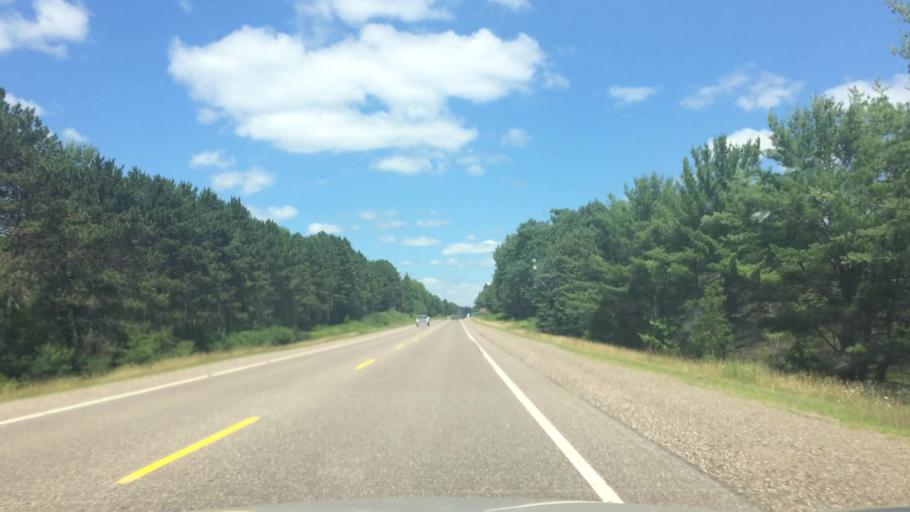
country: US
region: Wisconsin
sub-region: Vilas County
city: Lac du Flambeau
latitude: 45.9659
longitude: -89.7000
